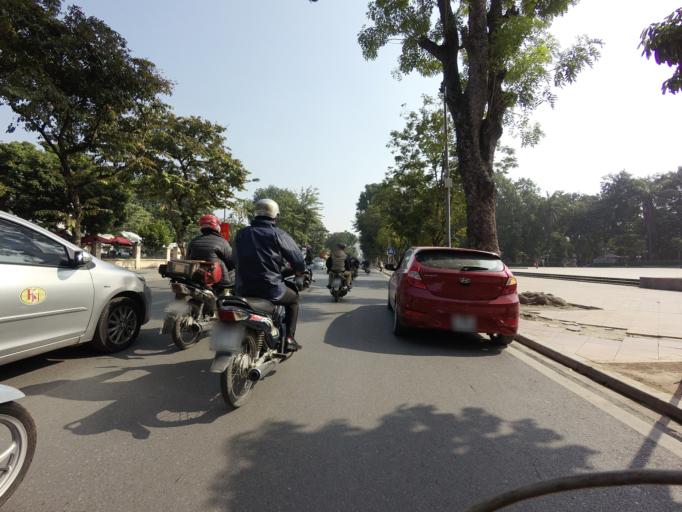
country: VN
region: Ha Noi
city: Hanoi
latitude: 21.0322
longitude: 105.8396
